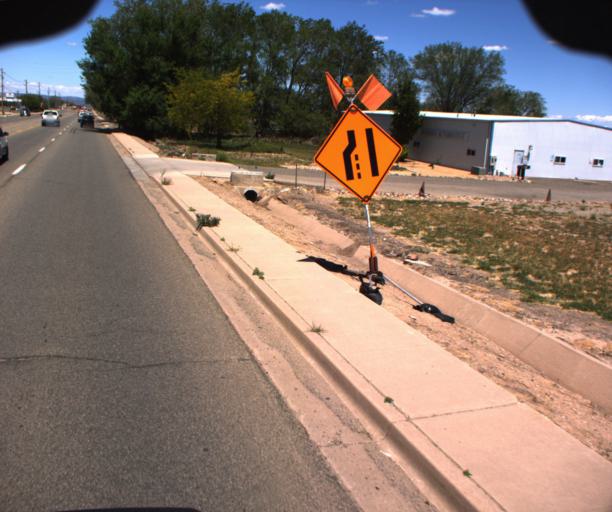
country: US
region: Arizona
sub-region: Yavapai County
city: Chino Valley
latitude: 34.7653
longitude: -112.4533
